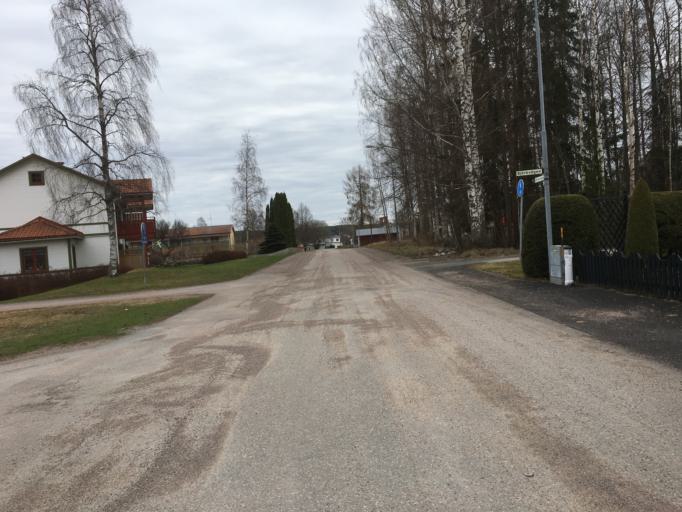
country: SE
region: Gaevleborg
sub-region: Hofors Kommun
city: Hofors
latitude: 60.5132
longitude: 16.4694
